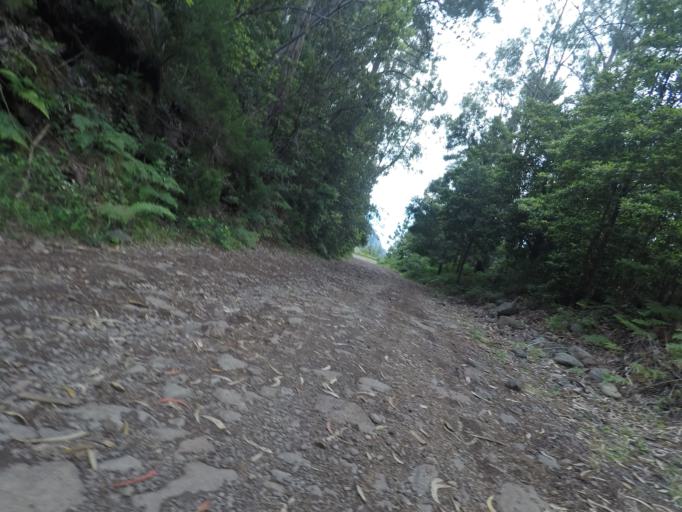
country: PT
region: Madeira
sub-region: Sao Vicente
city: Sao Vicente
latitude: 32.7776
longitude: -17.0480
